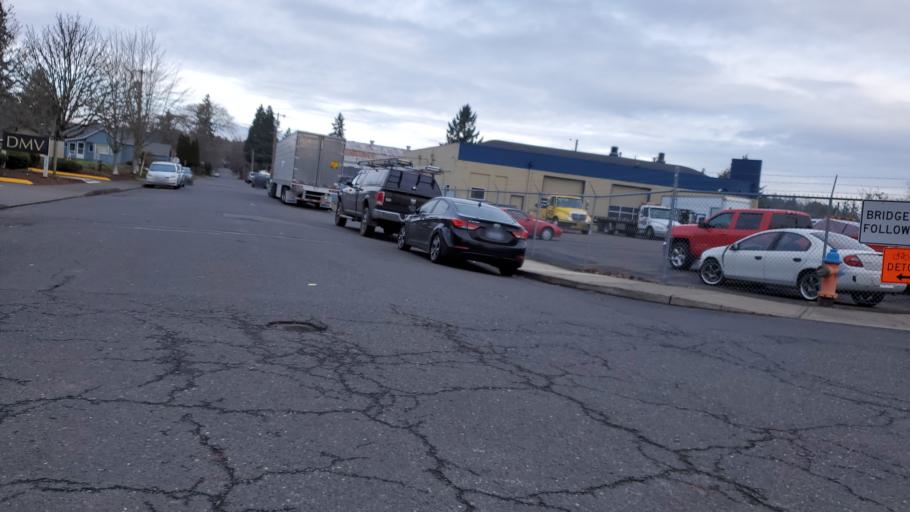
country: US
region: Oregon
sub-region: Clackamas County
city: Gladstone
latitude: 45.3797
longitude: -122.5843
